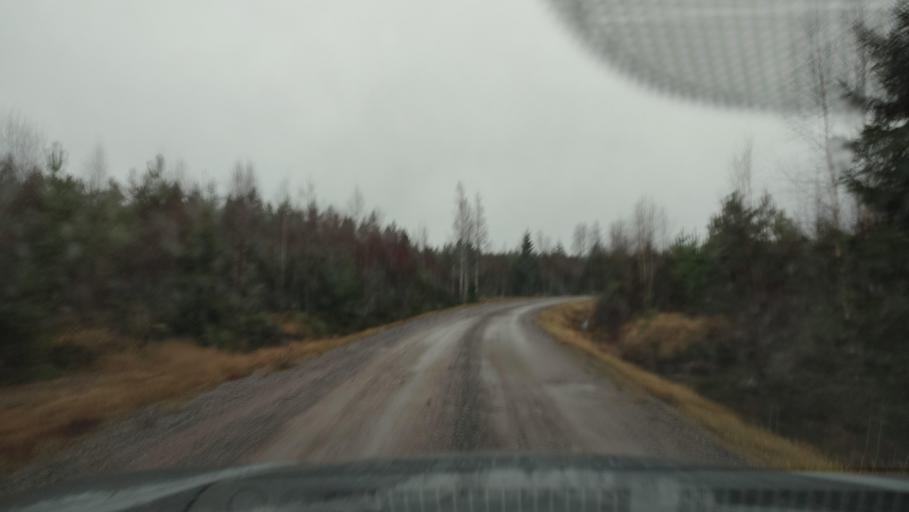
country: FI
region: Southern Ostrobothnia
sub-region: Suupohja
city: Karijoki
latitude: 62.2175
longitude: 21.7387
